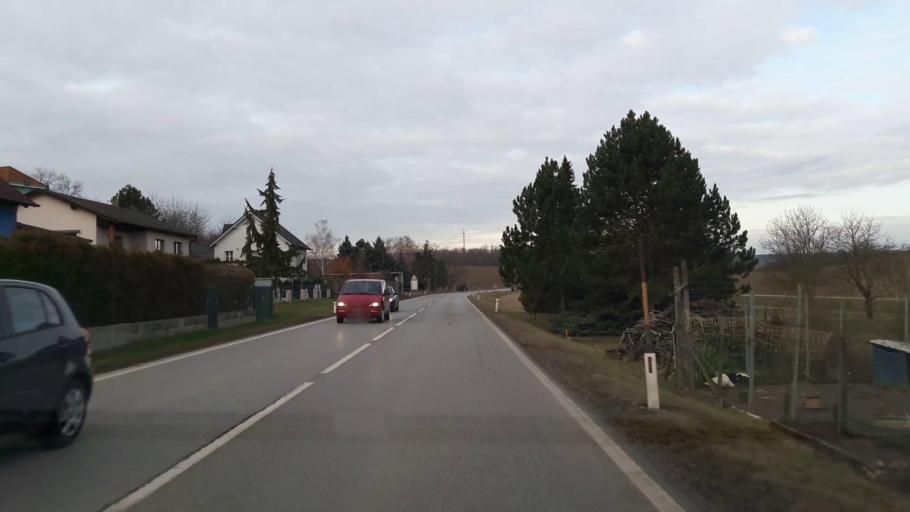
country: AT
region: Lower Austria
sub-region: Politischer Bezirk Mistelbach
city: Asparn an der Zaya
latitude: 48.6126
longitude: 16.5311
